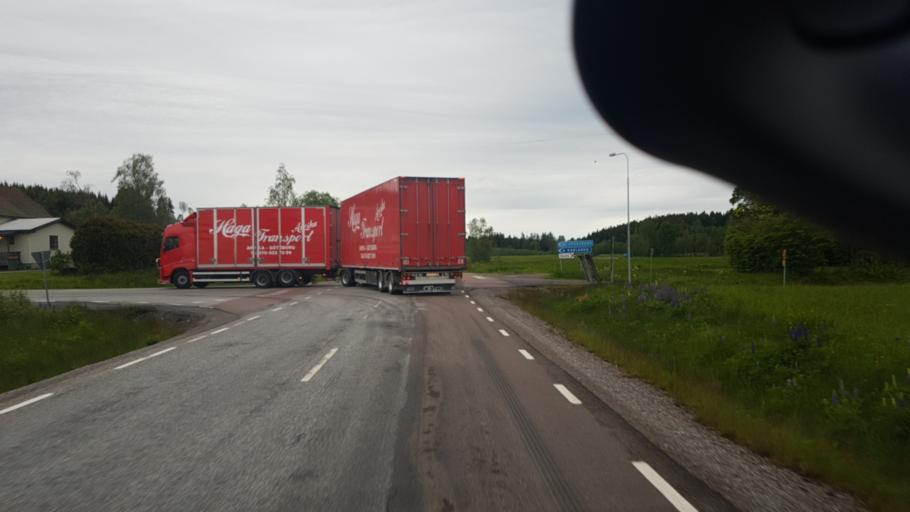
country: SE
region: Vaermland
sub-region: Arjangs Kommun
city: Arjaeng
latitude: 59.5564
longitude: 12.1191
